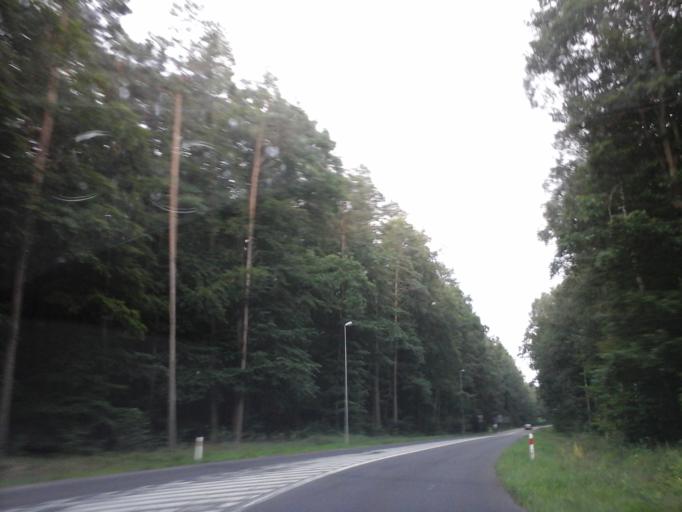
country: PL
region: West Pomeranian Voivodeship
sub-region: Powiat kamienski
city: Golczewo
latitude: 53.8072
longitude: 15.0107
